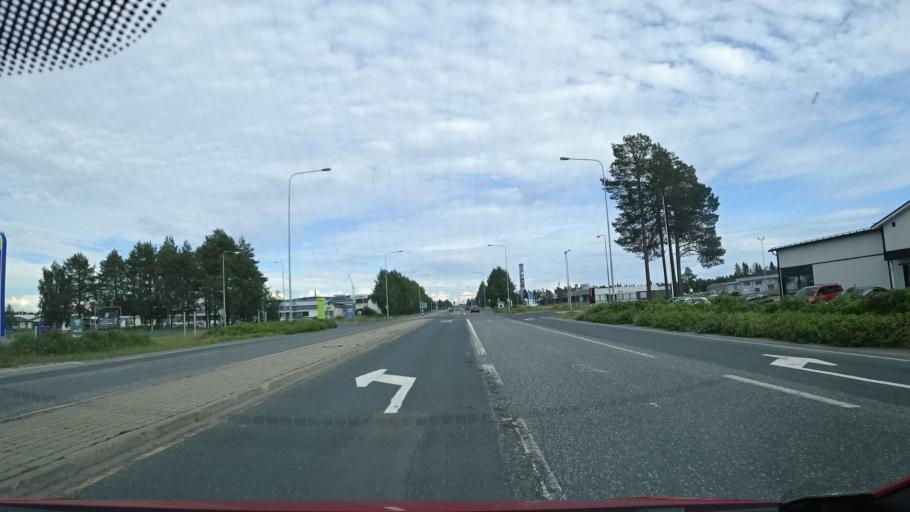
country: FI
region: Lapland
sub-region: Kemi-Tornio
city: Keminmaa
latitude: 65.7996
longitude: 24.5040
